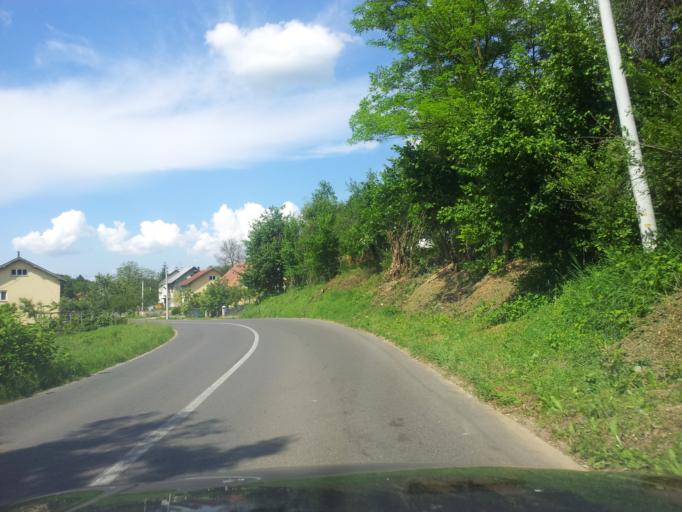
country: HR
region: Karlovacka
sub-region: Grad Karlovac
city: Karlovac
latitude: 45.4304
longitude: 15.4911
